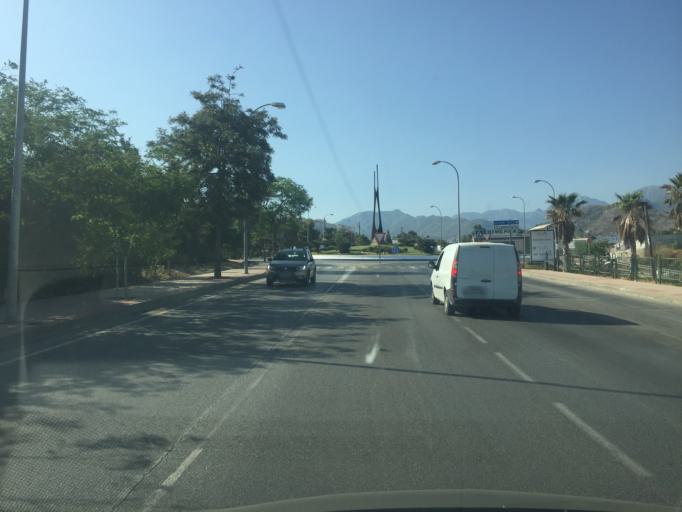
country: ES
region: Andalusia
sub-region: Provincia de Malaga
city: Nerja
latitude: 36.7569
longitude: -3.8860
